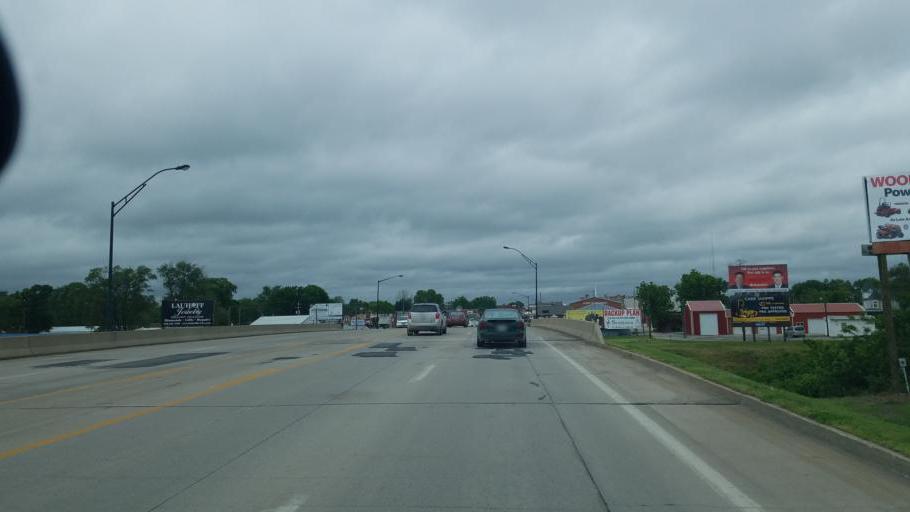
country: US
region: Missouri
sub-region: Livingston County
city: Chillicothe
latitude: 39.7862
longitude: -93.5531
